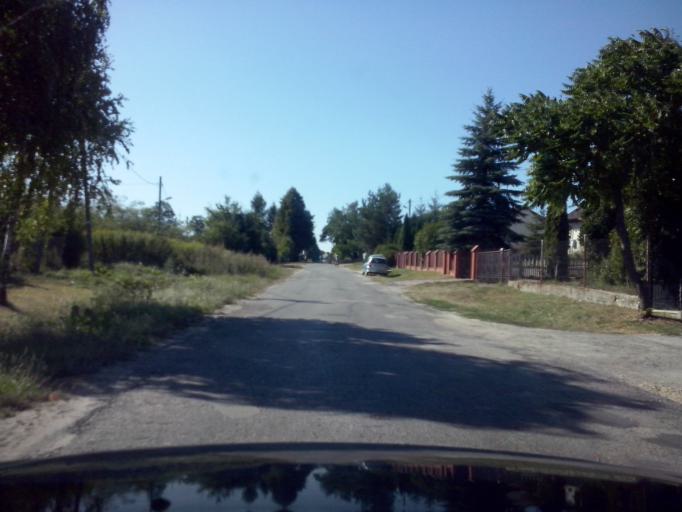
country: PL
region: Swietokrzyskie
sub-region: Powiat kielecki
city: Chmielnik
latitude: 50.6120
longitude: 20.7255
